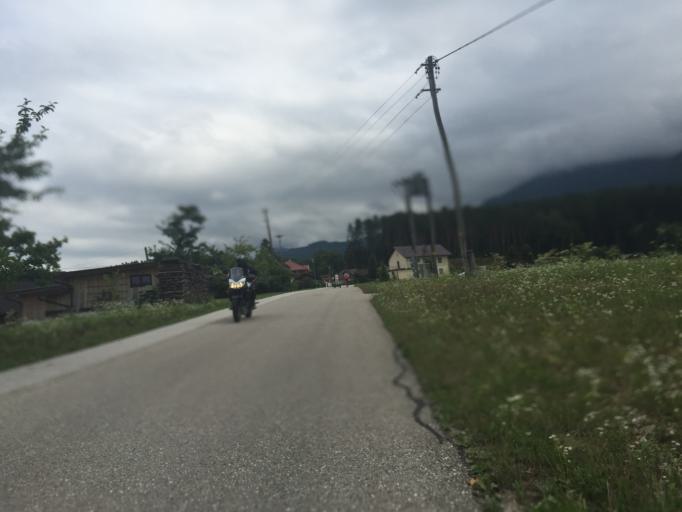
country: AT
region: Carinthia
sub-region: Politischer Bezirk Volkermarkt
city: Feistritz ob Bleiburg
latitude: 46.5595
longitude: 14.7641
